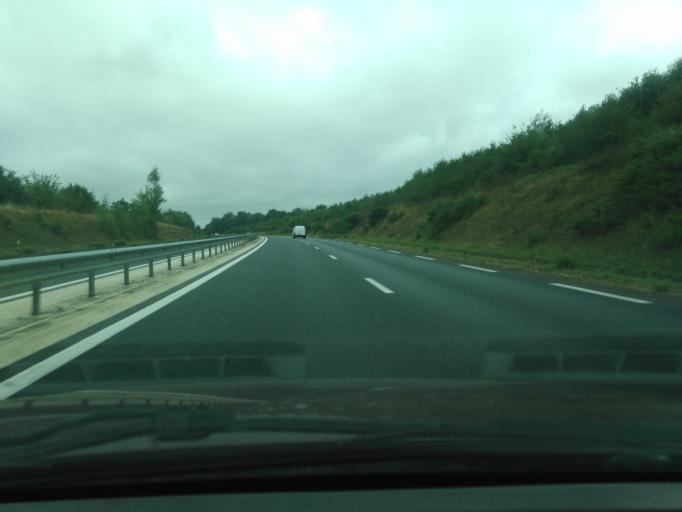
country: FR
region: Pays de la Loire
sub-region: Departement de la Vendee
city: La Roche-sur-Yon
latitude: 46.6796
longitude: -1.3750
